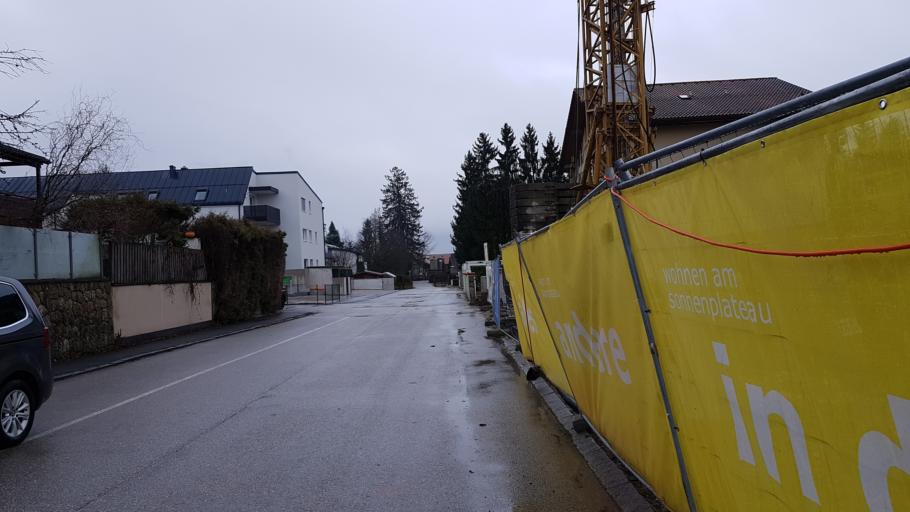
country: AT
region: Salzburg
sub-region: Politischer Bezirk Salzburg-Umgebung
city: Oberndorf bei Salzburg
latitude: 47.9413
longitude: 12.9494
